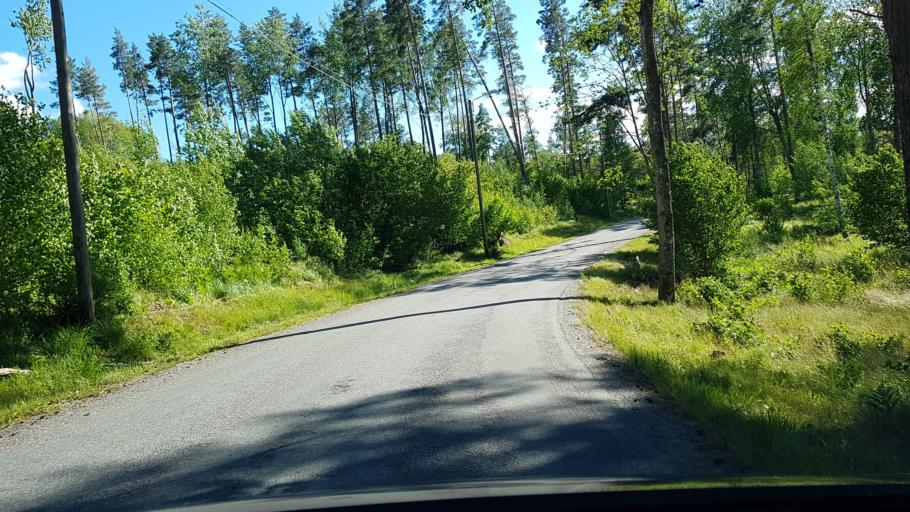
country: SE
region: Stockholm
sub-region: Upplands-Bro Kommun
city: Kungsaengen
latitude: 59.4853
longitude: 17.8032
